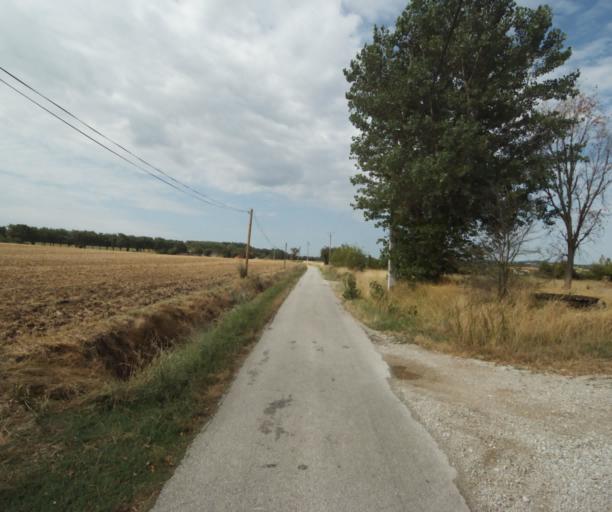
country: FR
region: Midi-Pyrenees
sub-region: Departement de la Haute-Garonne
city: Revel
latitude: 43.4514
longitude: 1.9623
